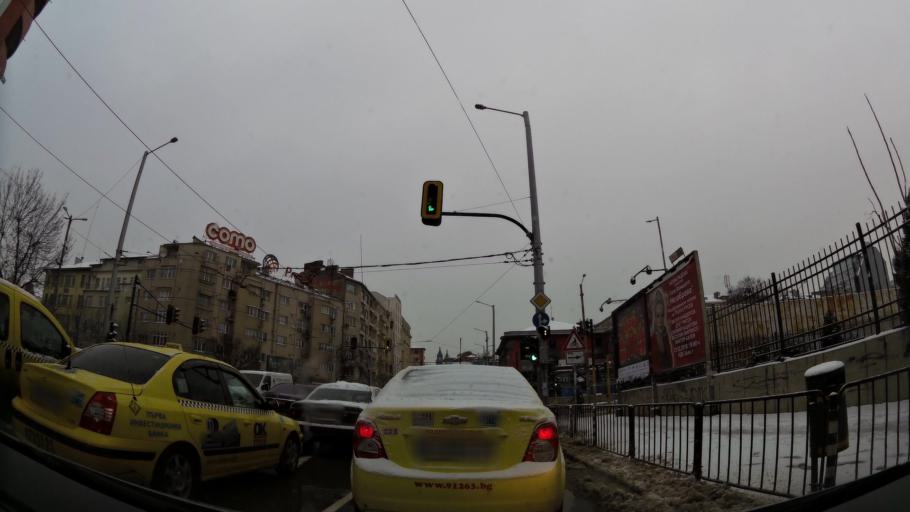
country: BG
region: Sofia-Capital
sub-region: Stolichna Obshtina
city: Sofia
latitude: 42.6992
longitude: 23.3156
